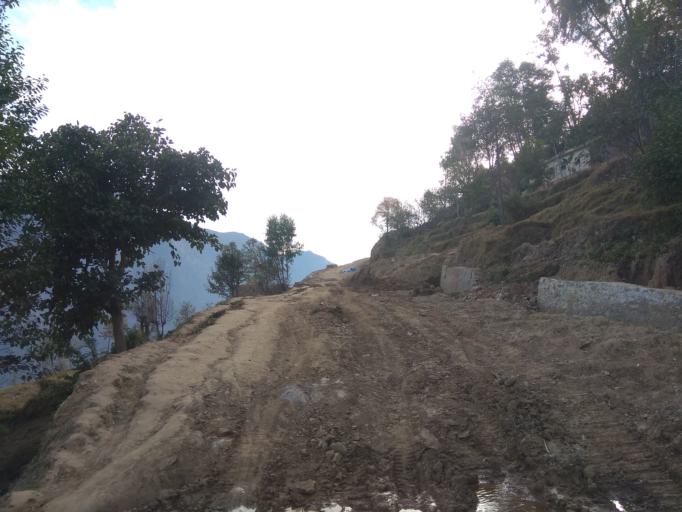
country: NP
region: Mid Western
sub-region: Bheri Zone
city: Dailekh
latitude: 29.2493
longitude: 81.6606
